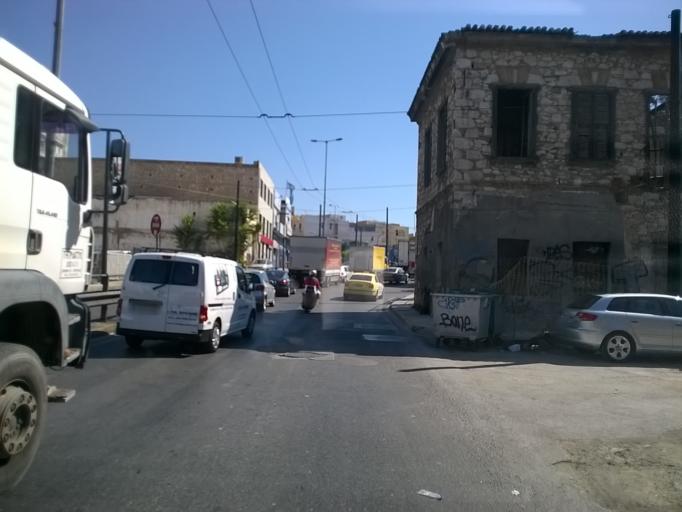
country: GR
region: Attica
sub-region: Nomos Attikis
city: Piraeus
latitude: 37.9489
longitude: 23.6460
